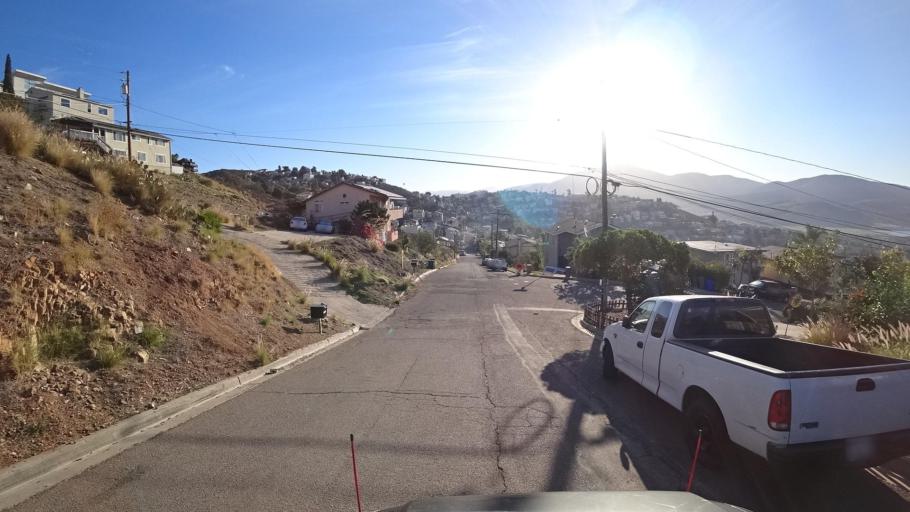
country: US
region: California
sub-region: San Diego County
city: La Presa
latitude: 32.7185
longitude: -116.9945
